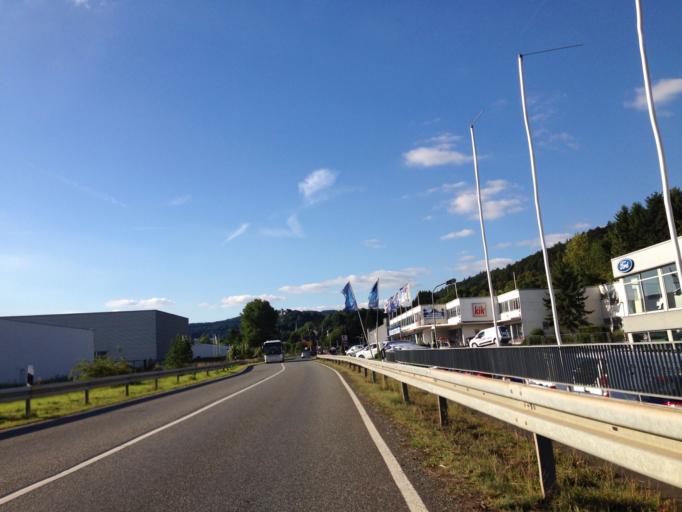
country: DE
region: Hesse
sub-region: Regierungsbezirk Giessen
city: Biedenkopf
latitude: 50.9013
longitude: 8.5405
